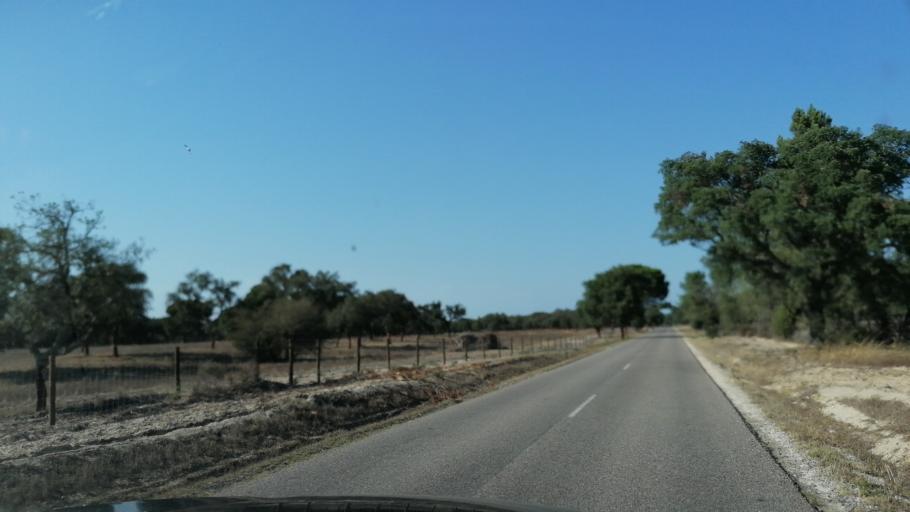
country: PT
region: Santarem
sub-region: Coruche
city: Coruche
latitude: 38.9189
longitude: -8.5243
